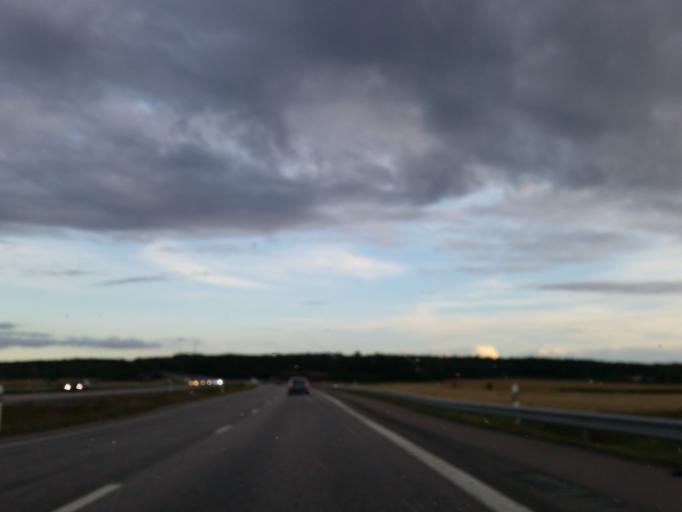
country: SE
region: Uppsala
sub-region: Uppsala Kommun
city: Saevja
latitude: 59.8121
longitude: 17.7560
